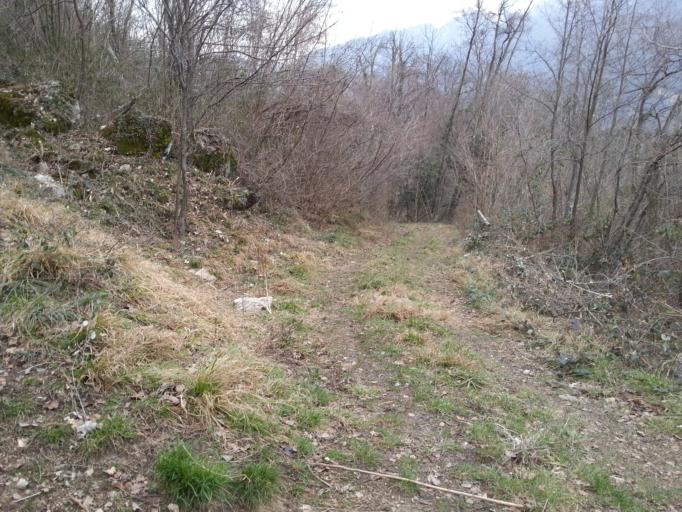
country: CH
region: Ticino
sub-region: Mendrisio District
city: Riva San Vitale
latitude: 45.8990
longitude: 8.9643
